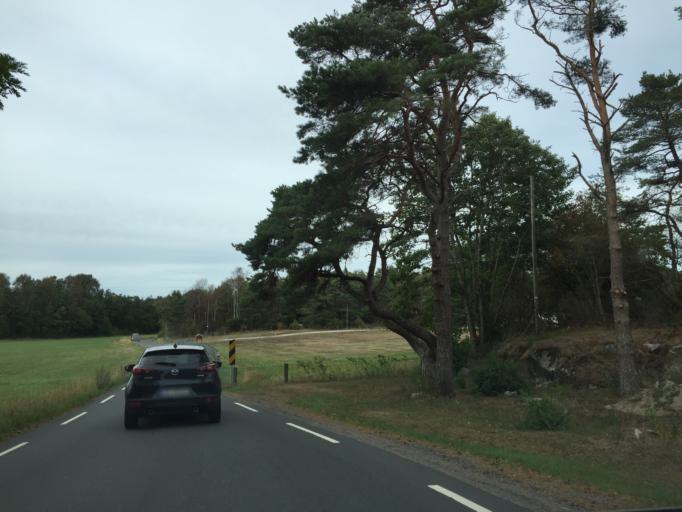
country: NO
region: Ostfold
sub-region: Hvaler
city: Skjaerhalden
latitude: 59.0374
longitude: 11.0279
